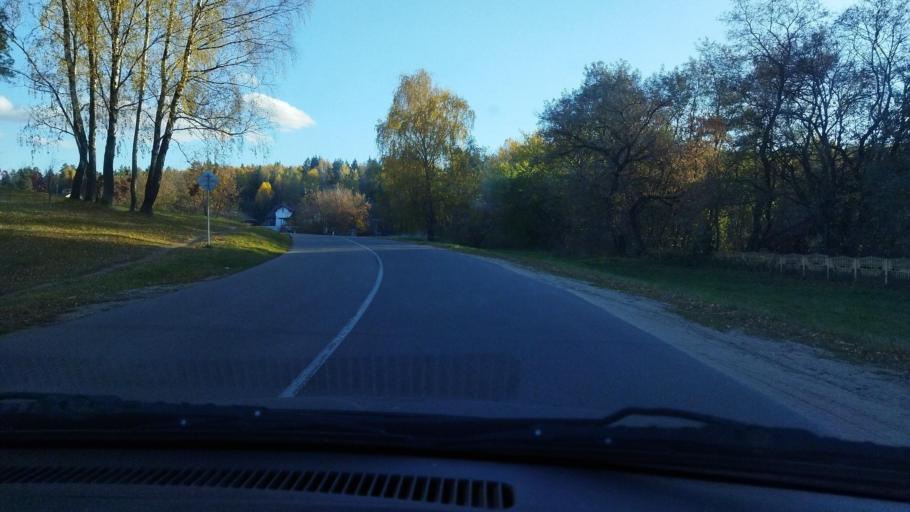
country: BY
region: Minsk
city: Slabada
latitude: 53.9743
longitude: 27.8566
